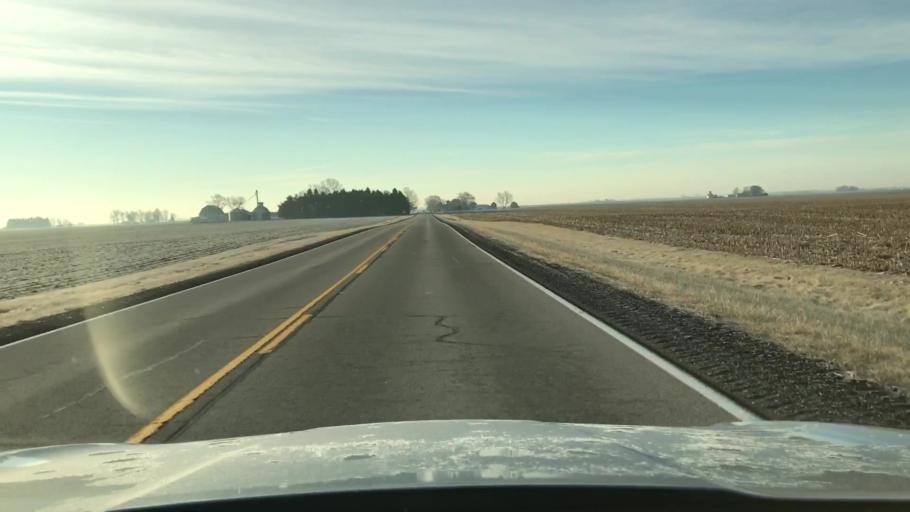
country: US
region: Illinois
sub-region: McLean County
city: Hudson
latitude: 40.6186
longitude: -88.9455
